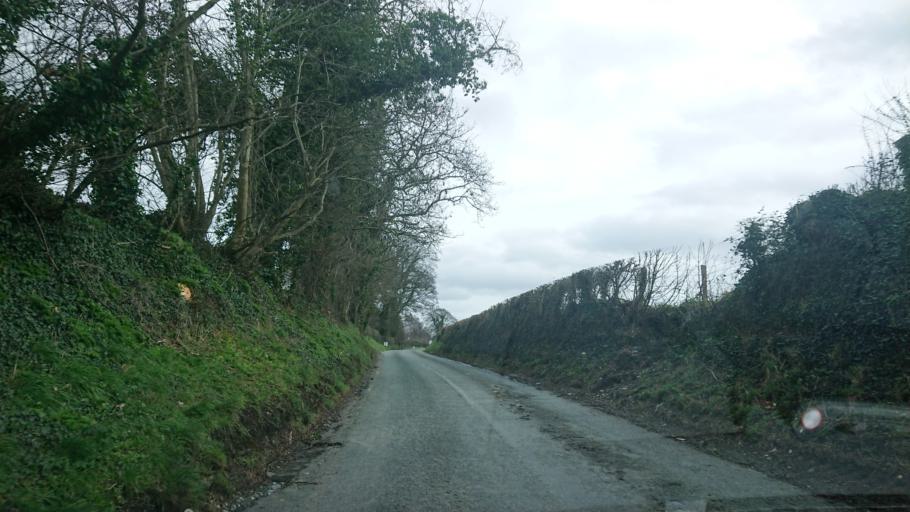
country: IE
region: Leinster
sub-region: Kildare
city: Naas
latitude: 53.2028
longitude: -6.6571
